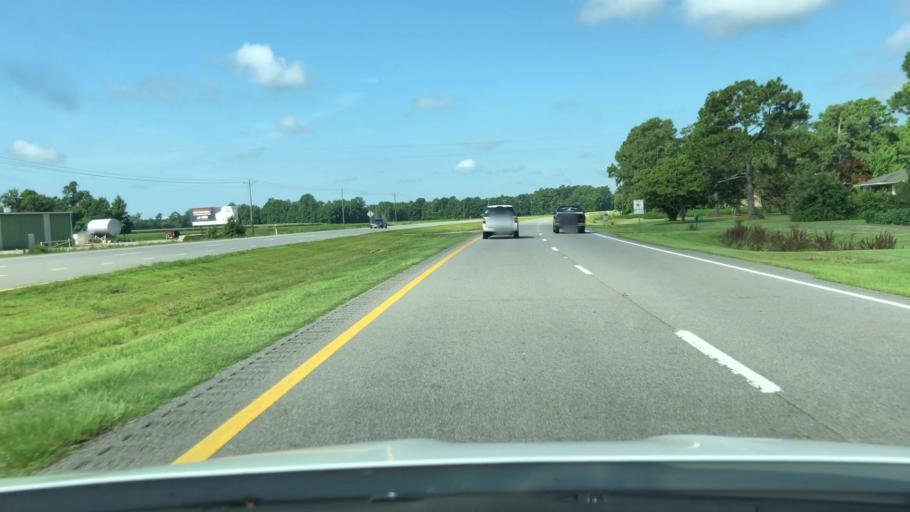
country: US
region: North Carolina
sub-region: Chowan County
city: Edenton
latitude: 36.0950
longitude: -76.5476
